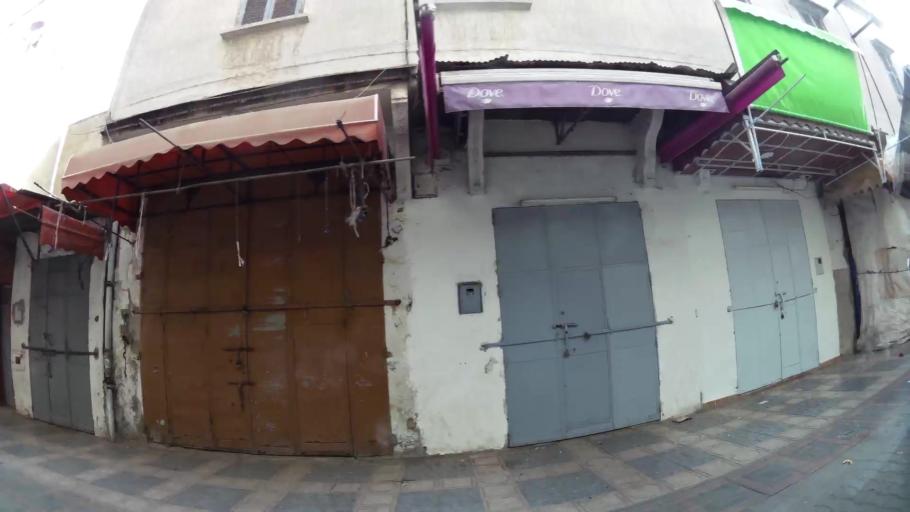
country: MA
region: Gharb-Chrarda-Beni Hssen
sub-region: Kenitra Province
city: Kenitra
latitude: 34.2633
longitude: -6.5629
